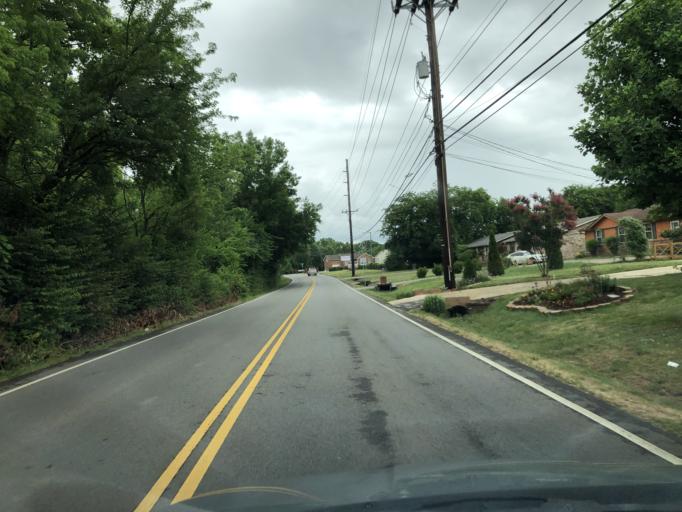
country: US
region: Tennessee
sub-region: Davidson County
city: Nashville
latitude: 36.2482
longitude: -86.7777
